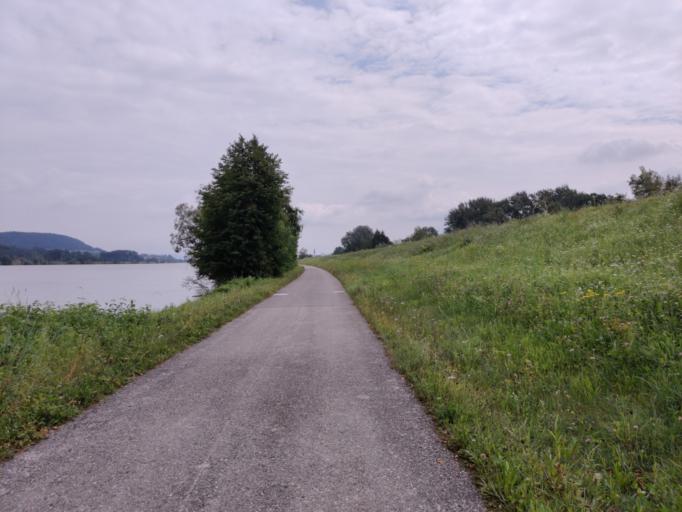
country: AT
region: Lower Austria
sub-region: Politischer Bezirk Melk
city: Pochlarn
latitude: 48.2138
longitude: 15.1883
